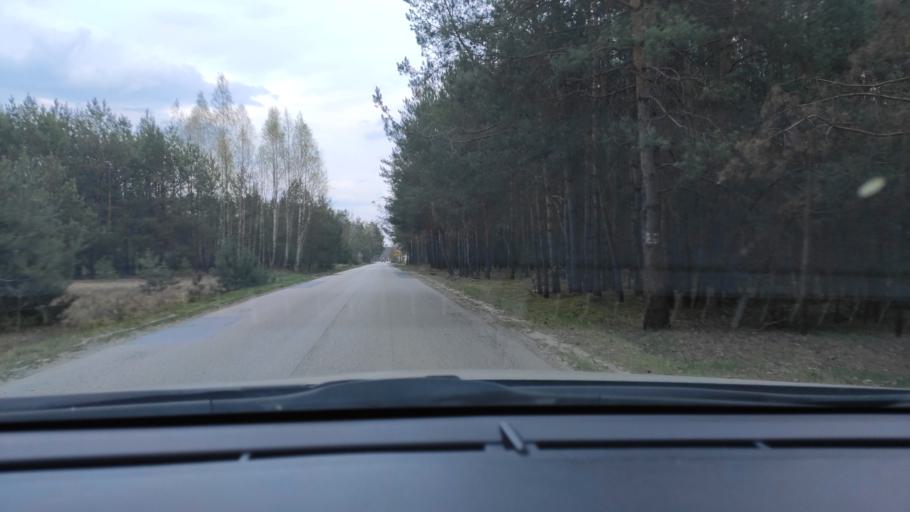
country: PL
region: Masovian Voivodeship
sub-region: Powiat radomski
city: Pionki
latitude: 51.5400
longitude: 21.3922
